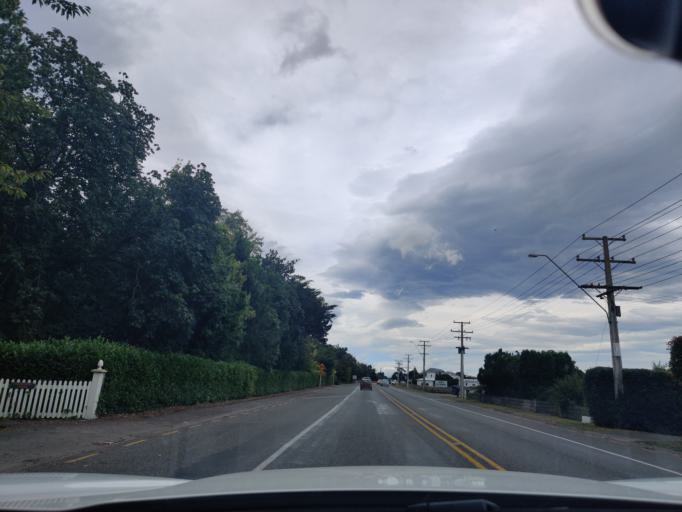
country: NZ
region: Wellington
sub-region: Masterton District
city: Masterton
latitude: -41.0166
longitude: 175.5352
